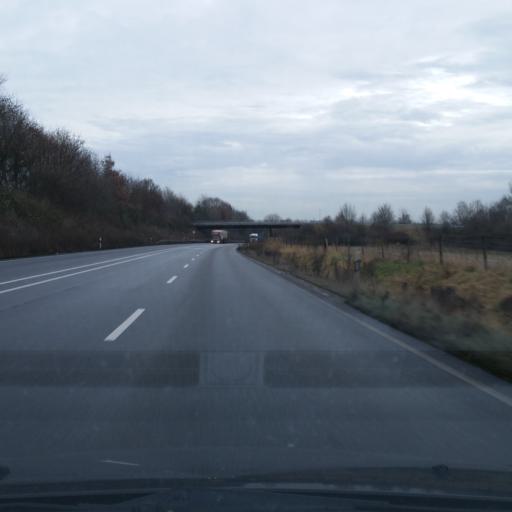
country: DE
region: North Rhine-Westphalia
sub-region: Regierungsbezirk Dusseldorf
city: Bocholt
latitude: 51.8148
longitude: 6.5892
